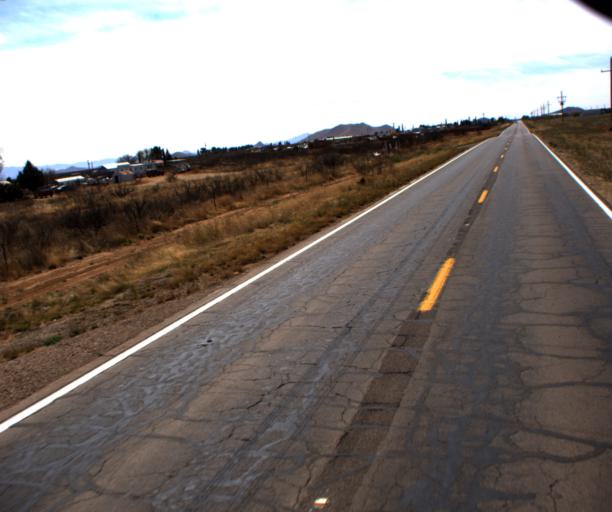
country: US
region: Arizona
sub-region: Cochise County
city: Willcox
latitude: 31.9626
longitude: -109.8422
